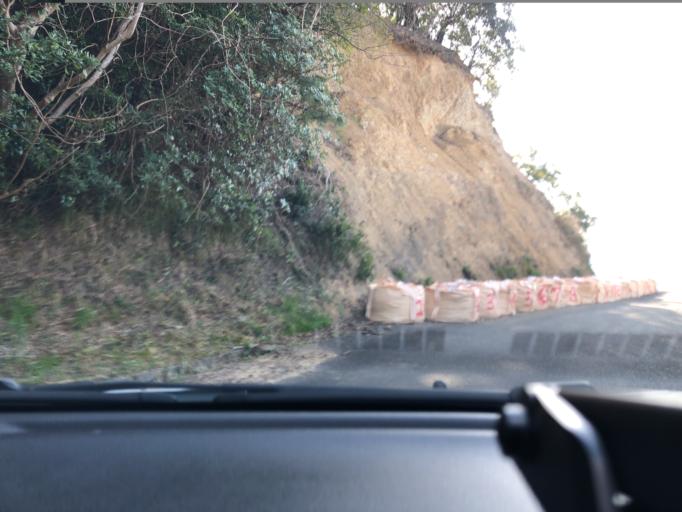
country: JP
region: Kochi
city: Sukumo
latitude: 32.9133
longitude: 132.6893
